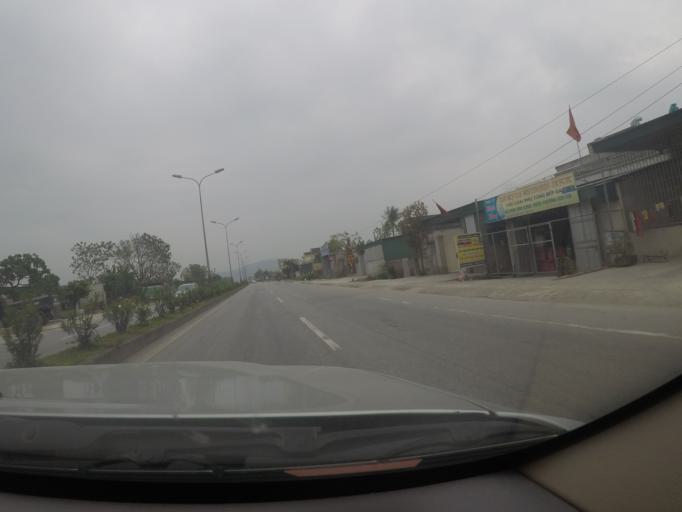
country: VN
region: Nghe An
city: Dien Chau
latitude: 18.9377
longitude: 105.6053
